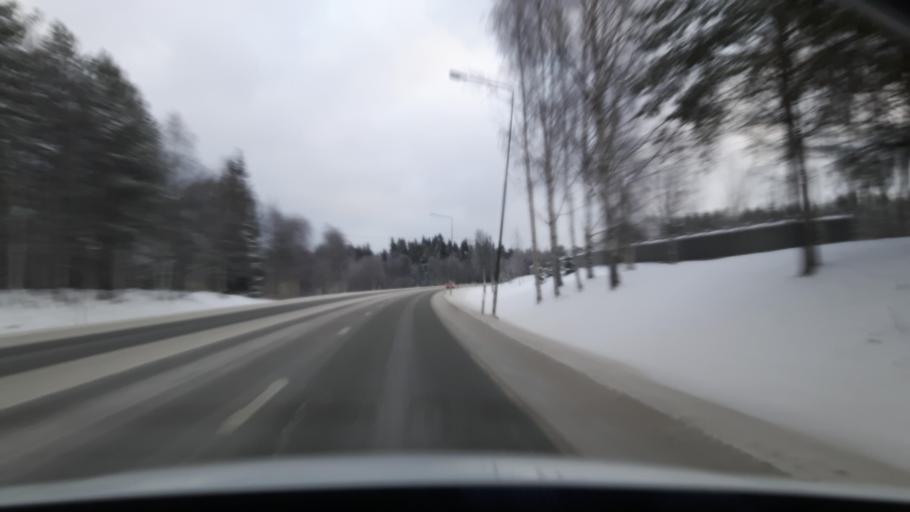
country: SE
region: Vaesterbotten
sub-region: Umea Kommun
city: Umea
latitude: 63.8454
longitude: 20.2804
